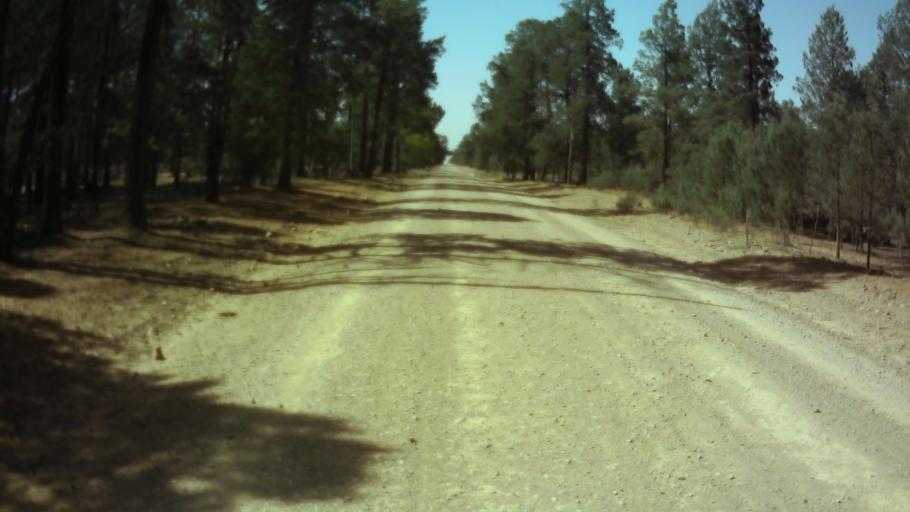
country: AU
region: New South Wales
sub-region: Weddin
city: Grenfell
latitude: -33.9661
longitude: 147.9312
